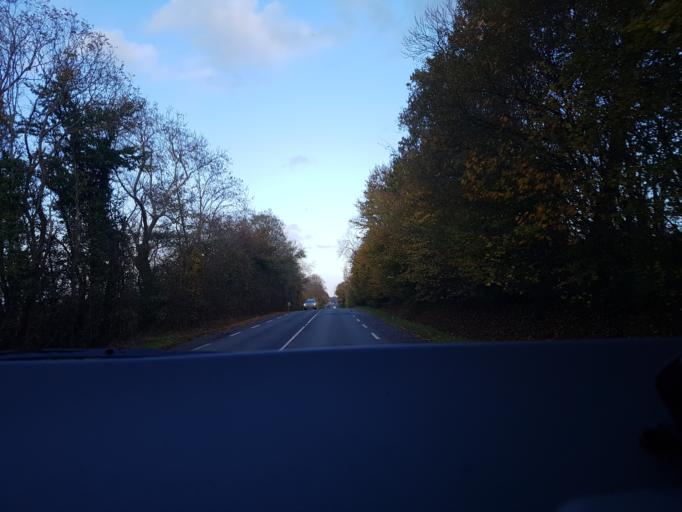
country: FR
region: Lower Normandy
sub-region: Departement du Calvados
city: Dozule
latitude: 49.2270
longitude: -0.0583
